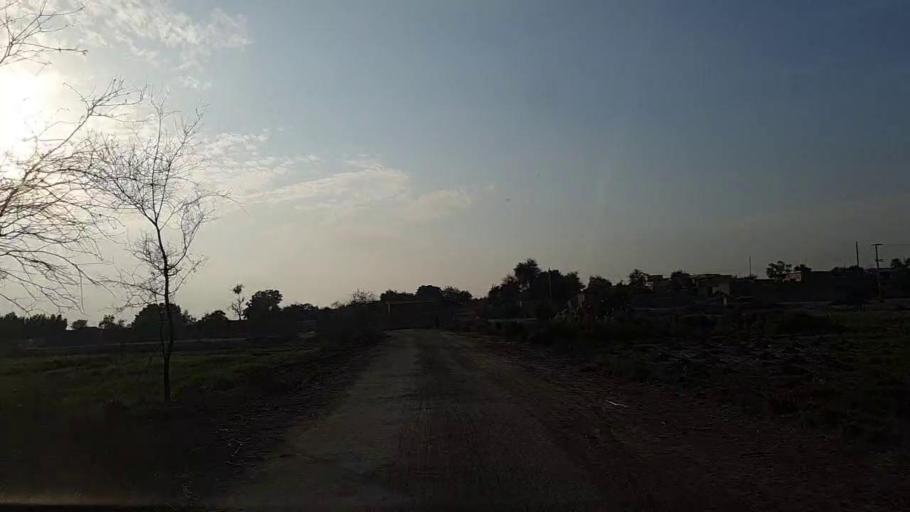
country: PK
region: Sindh
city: Jam Sahib
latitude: 26.3955
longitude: 68.5247
